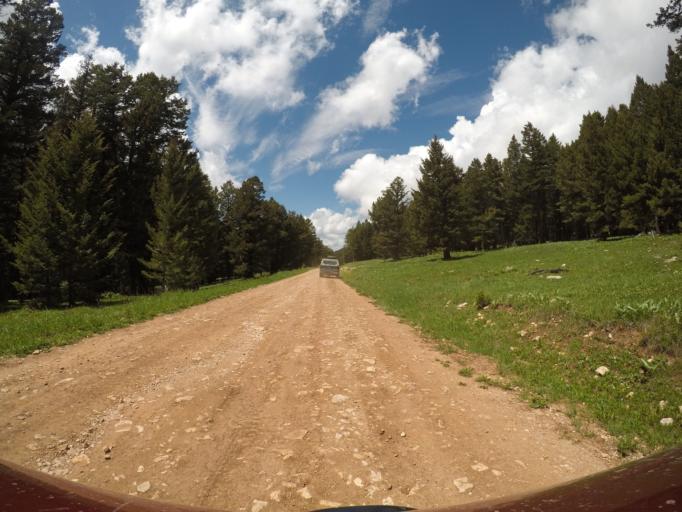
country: US
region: Wyoming
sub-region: Big Horn County
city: Lovell
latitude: 45.1638
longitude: -108.4059
